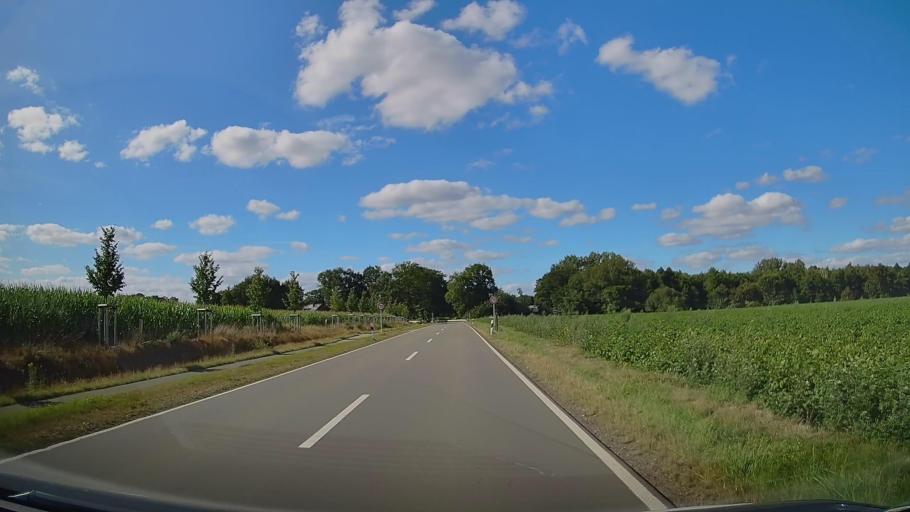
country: DE
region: Lower Saxony
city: Loningen
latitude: 52.7029
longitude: 7.7577
